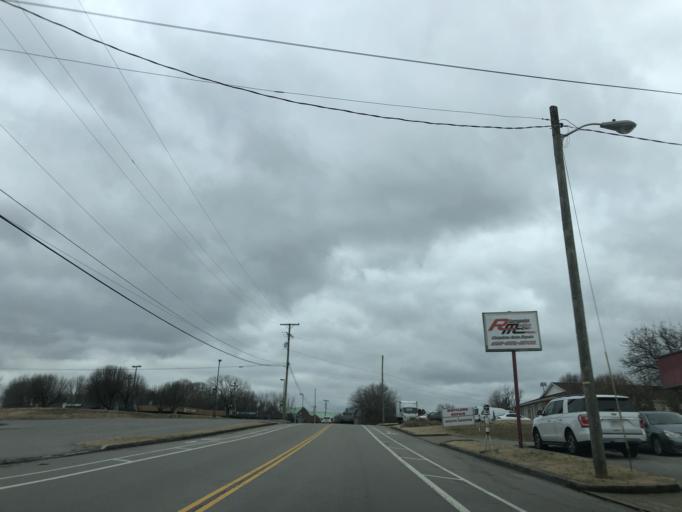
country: US
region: Tennessee
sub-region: Davidson County
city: Goodlettsville
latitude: 36.2968
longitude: -86.7026
